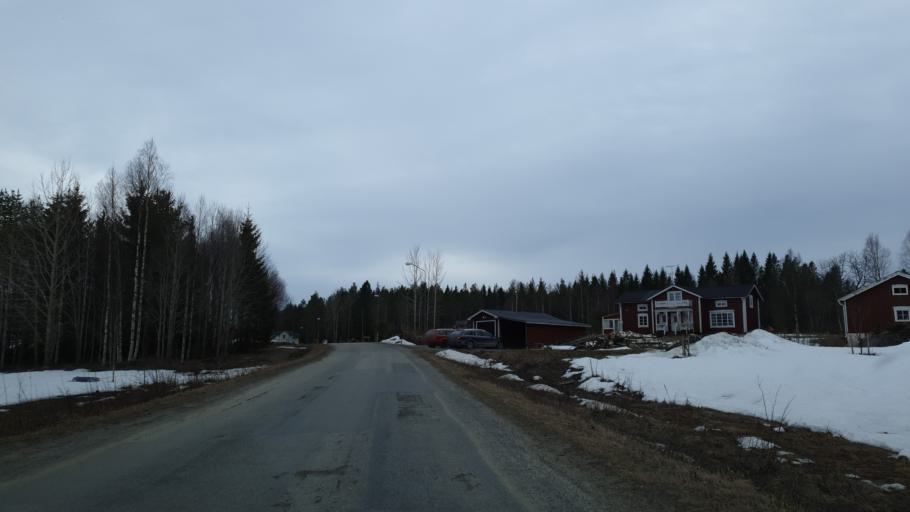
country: SE
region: Vaesterbotten
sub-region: Robertsfors Kommun
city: Robertsfors
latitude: 64.3963
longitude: 21.0022
